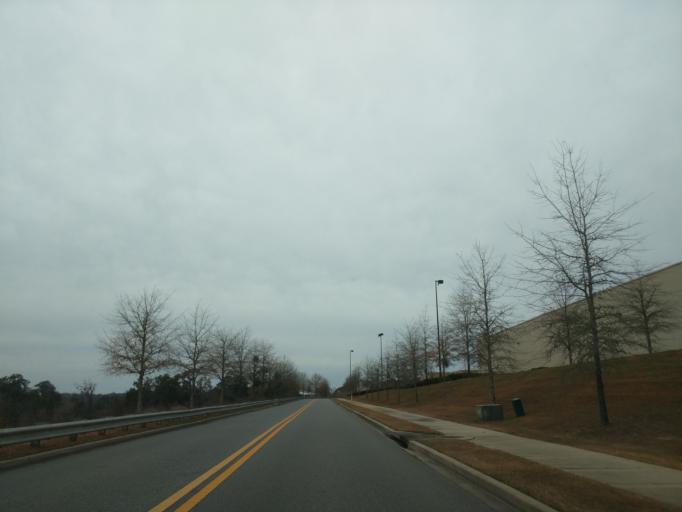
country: US
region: Florida
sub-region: Leon County
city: Tallahassee
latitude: 30.4598
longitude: -84.2117
